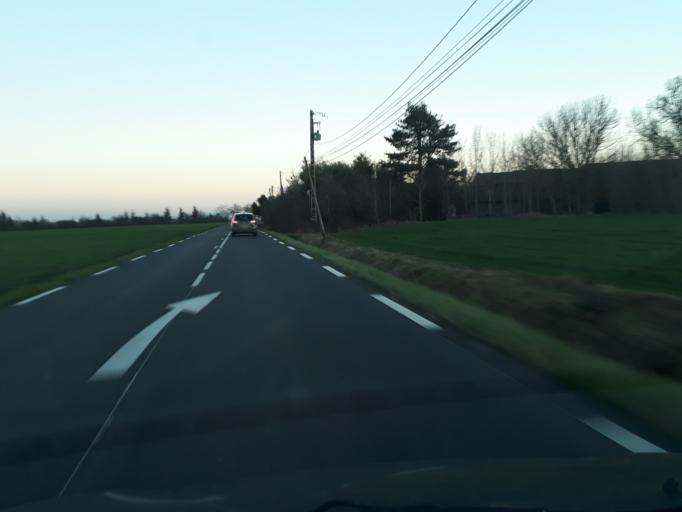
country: FR
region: Midi-Pyrenees
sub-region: Departement de la Haute-Garonne
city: Saint-Lys
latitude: 43.5331
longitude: 1.1686
